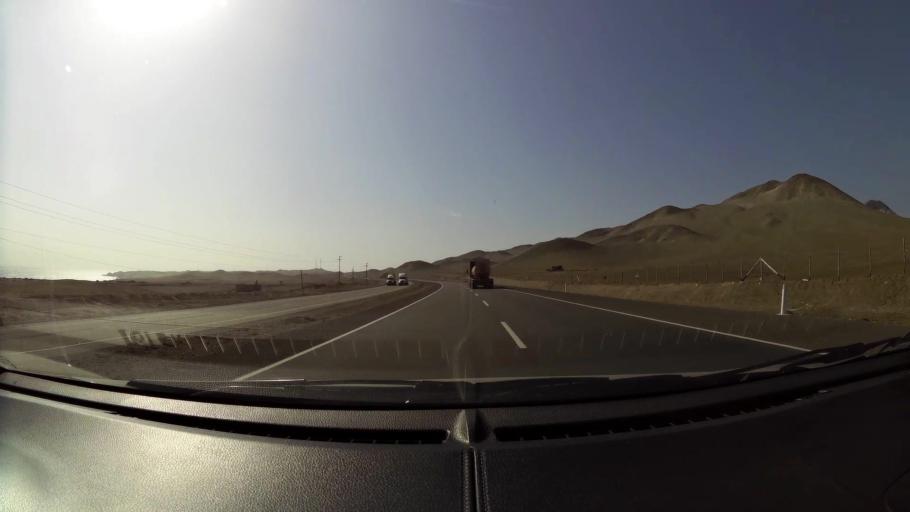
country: PE
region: Ancash
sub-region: Provincia de Huarmey
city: La Caleta Culebras
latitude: -9.9707
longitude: -78.2020
